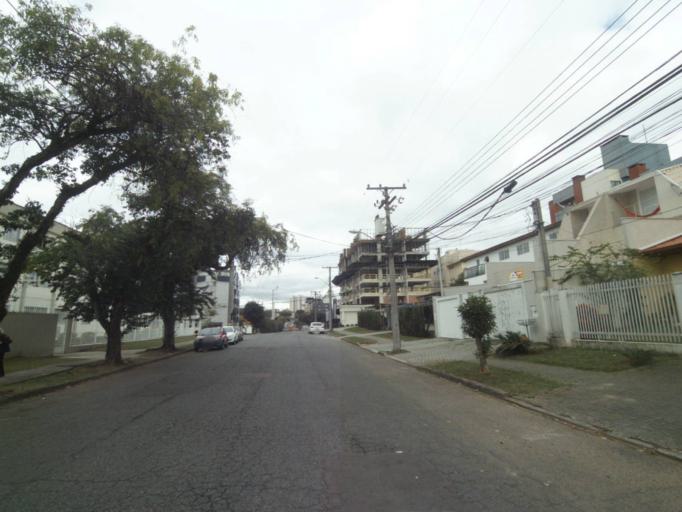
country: BR
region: Parana
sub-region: Curitiba
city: Curitiba
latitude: -25.4639
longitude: -49.2867
